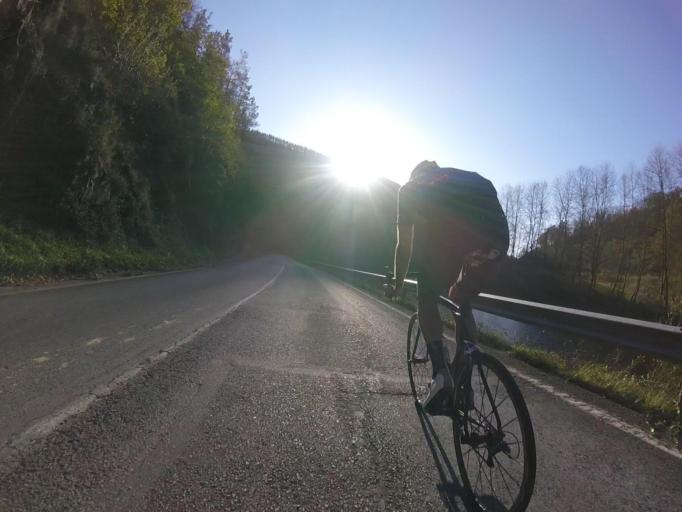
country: ES
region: Navarre
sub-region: Provincia de Navarra
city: Igantzi
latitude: 43.2348
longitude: -1.6760
